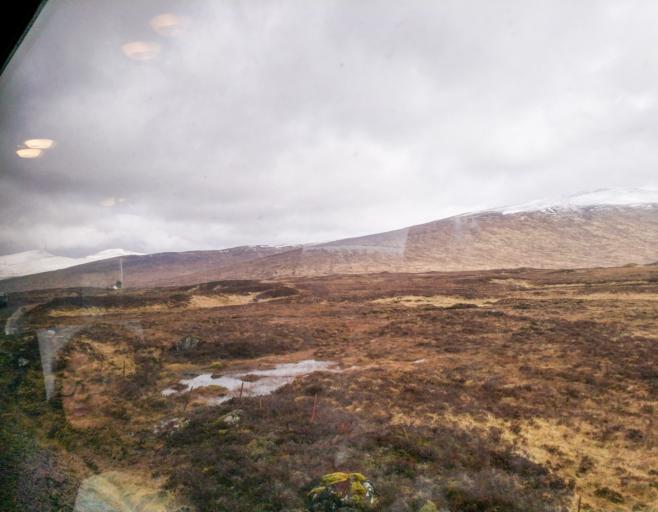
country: GB
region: Scotland
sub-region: Highland
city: Spean Bridge
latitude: 56.7535
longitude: -4.6827
